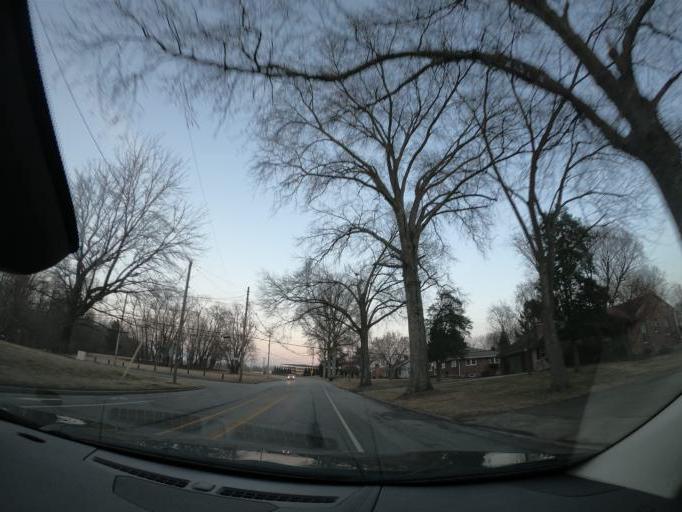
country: US
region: Kentucky
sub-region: Jefferson County
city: Lyndon
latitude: 38.2559
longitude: -85.5888
